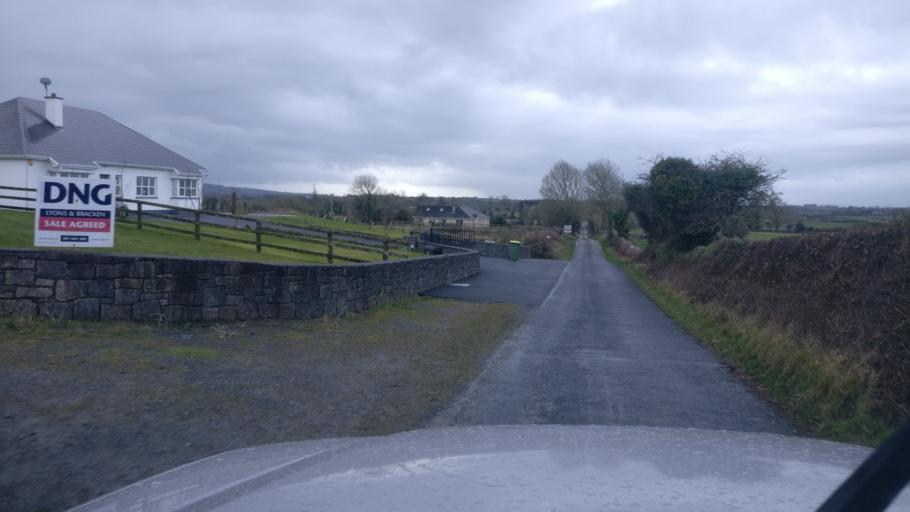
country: IE
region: Connaught
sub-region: County Galway
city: Athenry
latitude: 53.1942
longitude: -8.6859
